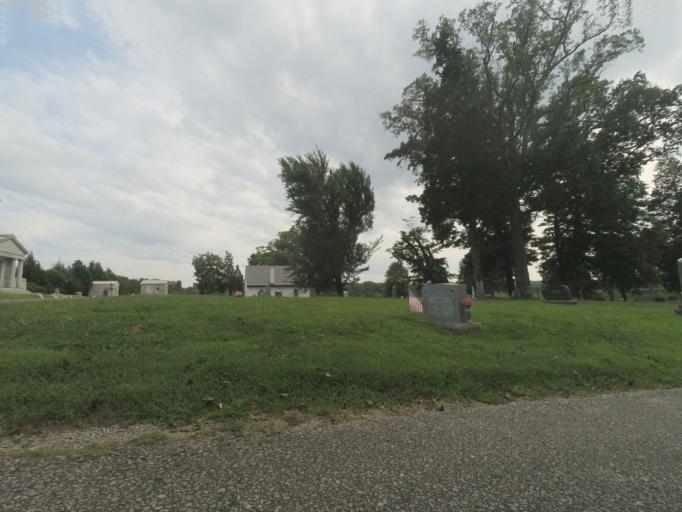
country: US
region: West Virginia
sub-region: Cabell County
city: Huntington
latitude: 38.4103
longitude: -82.4127
